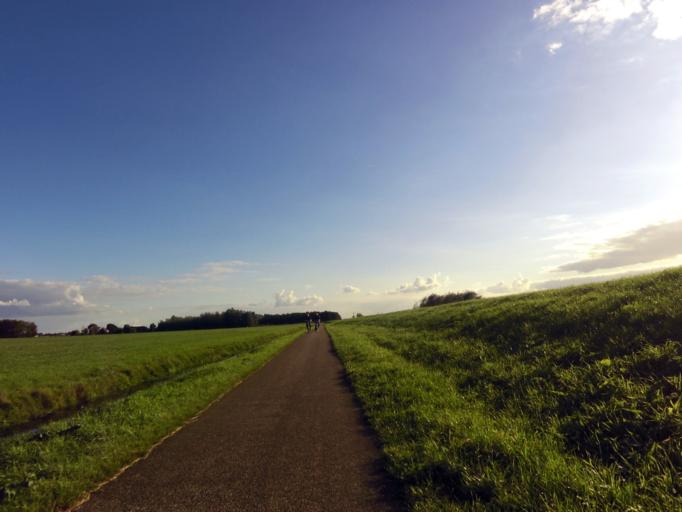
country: NL
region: South Holland
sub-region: Gemeente Alphen aan den Rijn
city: Alphen aan den Rijn
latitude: 52.1200
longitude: 4.6037
